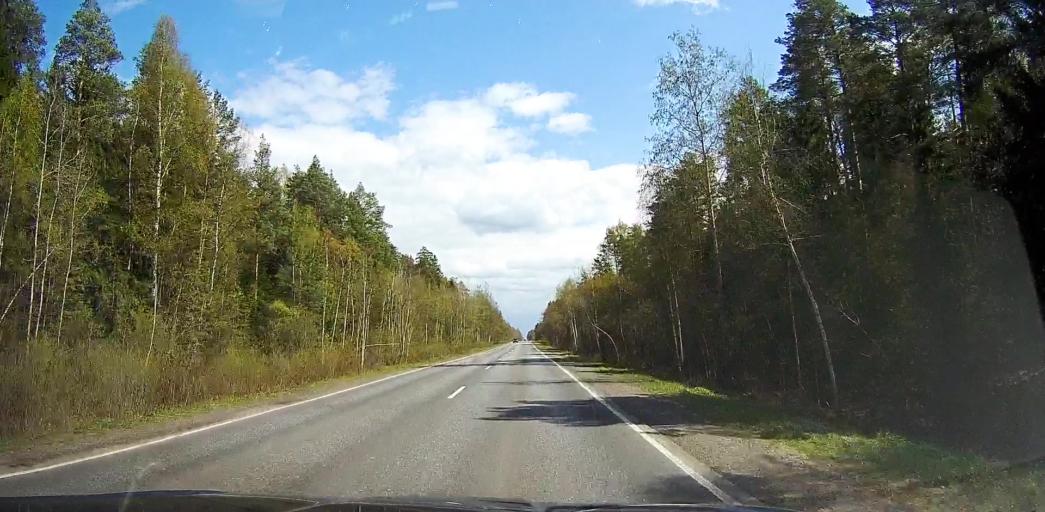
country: RU
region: Moskovskaya
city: Imeni Tsyurupy
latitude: 55.5517
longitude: 38.7266
